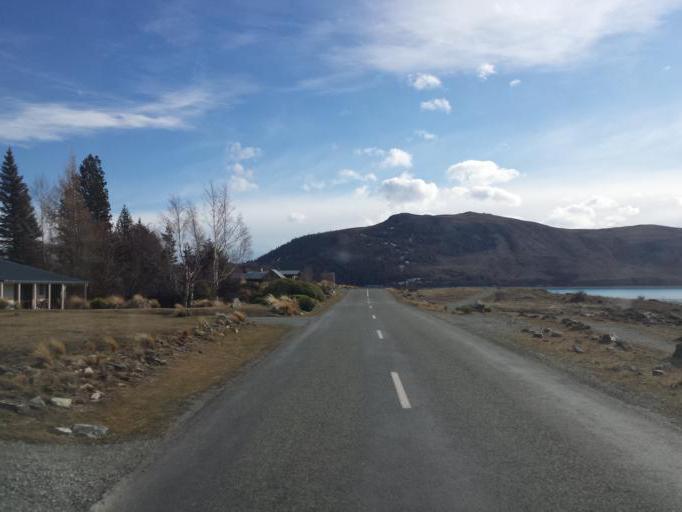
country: NZ
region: Canterbury
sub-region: Timaru District
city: Pleasant Point
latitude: -44.0055
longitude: 170.4866
